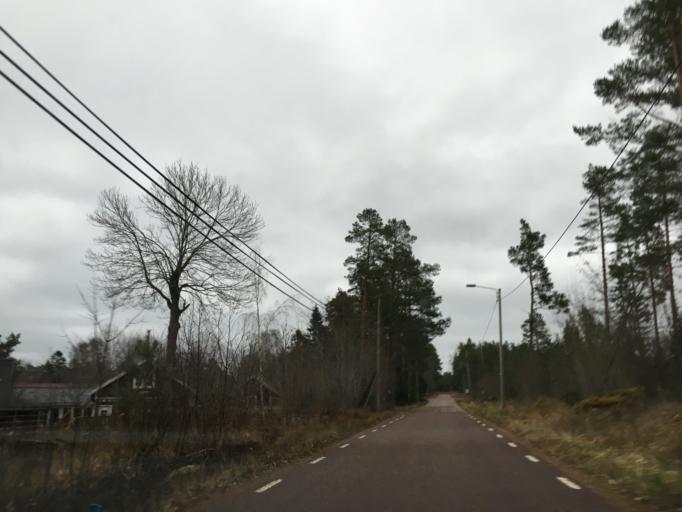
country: SE
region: Uppsala
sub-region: Alvkarleby Kommun
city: AElvkarleby
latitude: 60.6468
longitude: 17.5436
